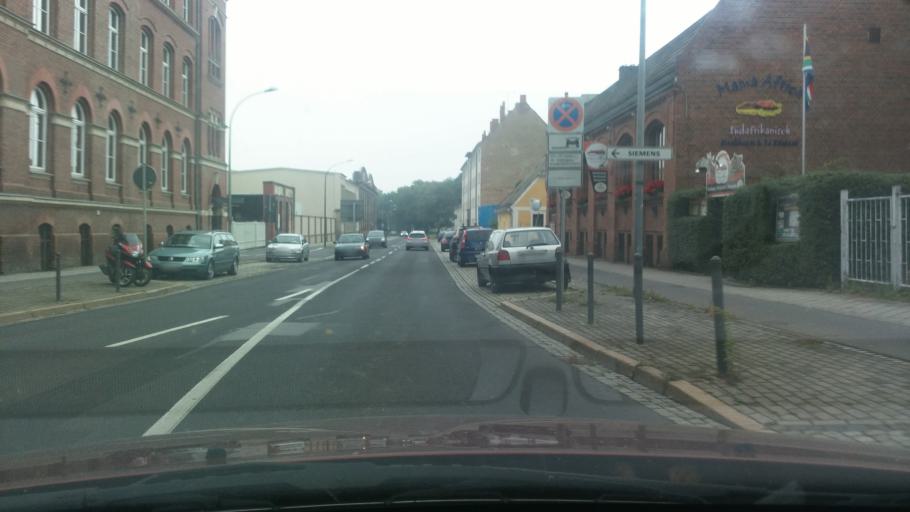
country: DE
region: Saxony
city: Goerlitz
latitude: 51.1465
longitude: 14.9713
